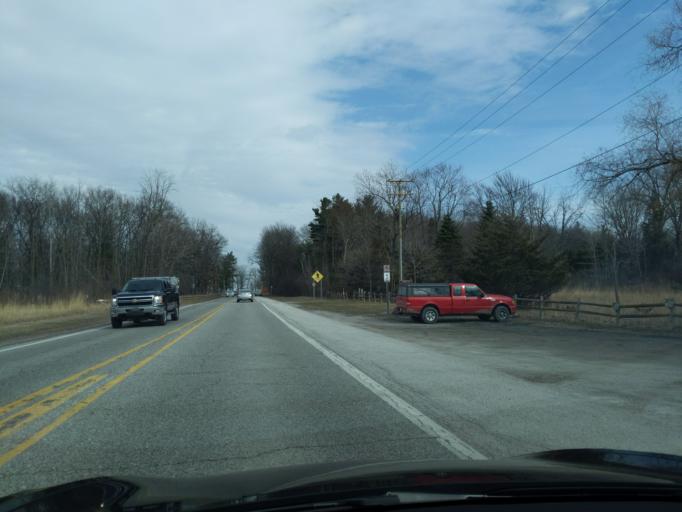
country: US
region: Michigan
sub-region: Bay County
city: Bay City
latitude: 43.6671
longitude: -83.9106
